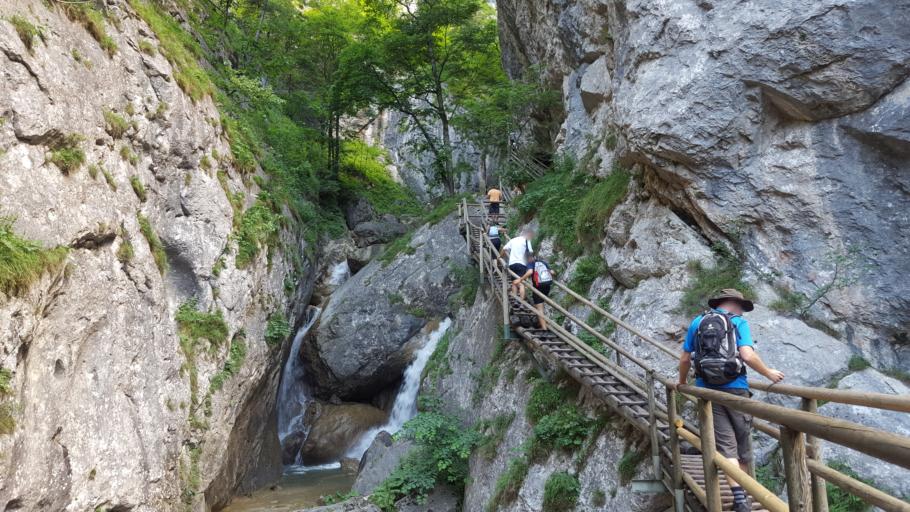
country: AT
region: Styria
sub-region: Politischer Bezirk Graz-Umgebung
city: Rothelstein
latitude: 47.3434
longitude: 15.3989
